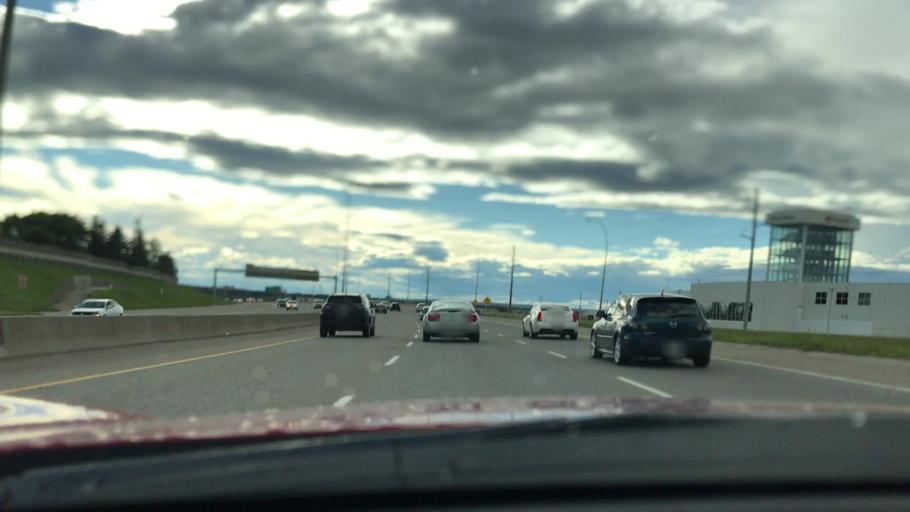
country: CA
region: Alberta
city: Calgary
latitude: 50.9454
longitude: -113.9831
